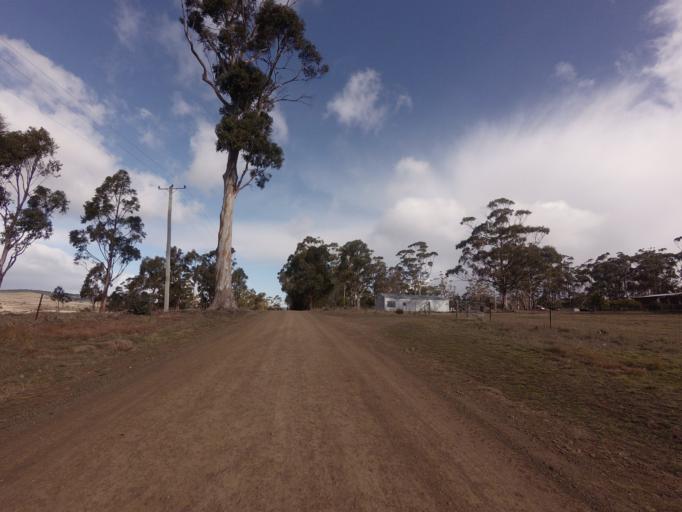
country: AU
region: Tasmania
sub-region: Sorell
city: Sorell
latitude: -42.3289
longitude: 147.9678
